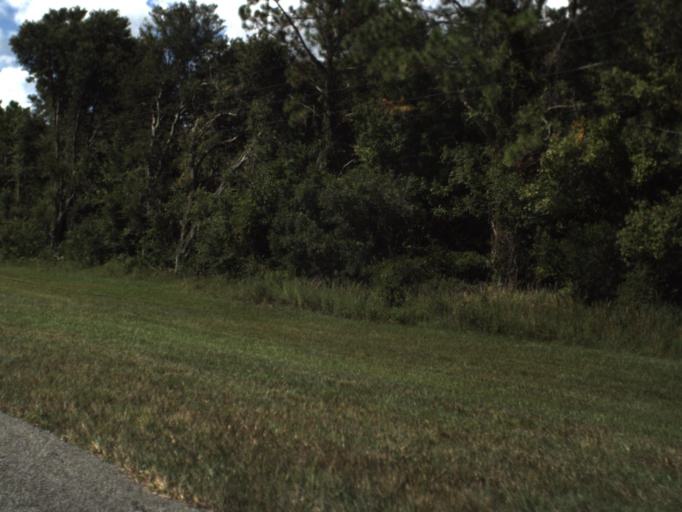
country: US
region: Florida
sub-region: Pasco County
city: Zephyrhills North
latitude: 28.2882
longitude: -82.0555
